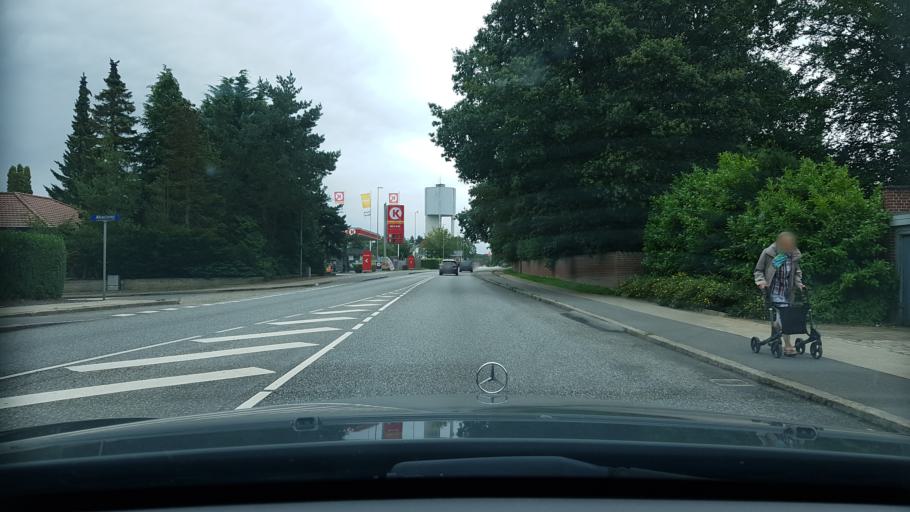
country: DK
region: Central Jutland
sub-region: Randers Kommune
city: Randers
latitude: 56.4766
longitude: 10.0414
